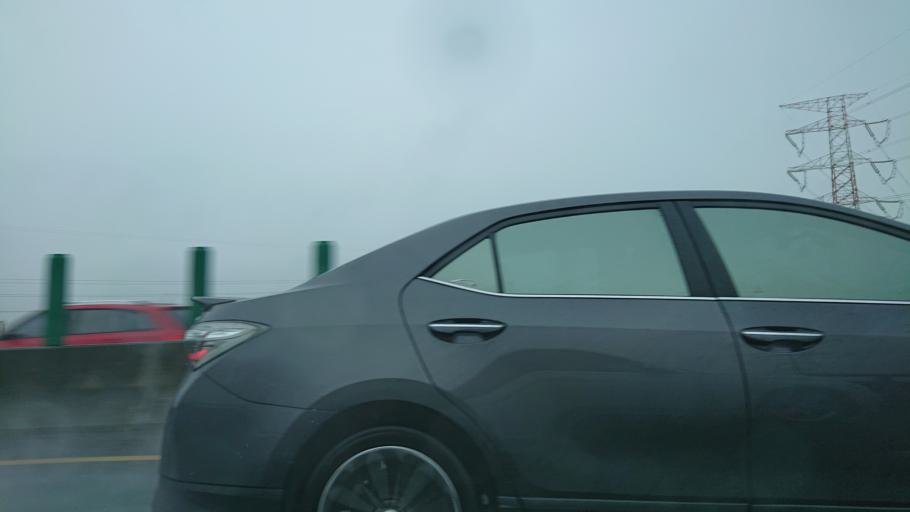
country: TW
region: Taiwan
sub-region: Yunlin
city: Douliu
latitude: 23.7785
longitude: 120.2737
